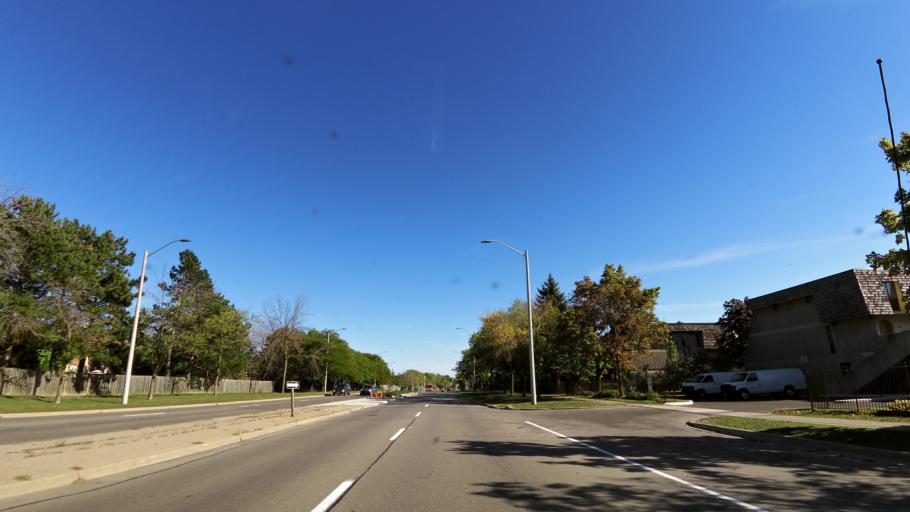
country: CA
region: Ontario
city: Mississauga
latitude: 43.6005
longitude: -79.6255
